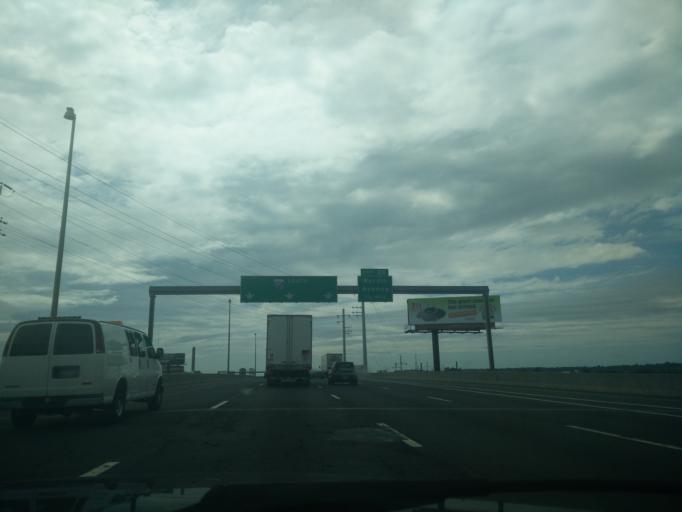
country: US
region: Connecticut
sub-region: Fairfield County
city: Bridgeport
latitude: 41.1696
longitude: -73.1967
